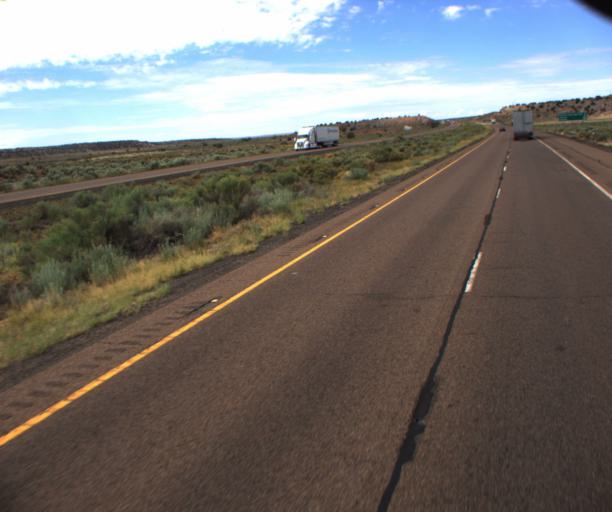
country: US
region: Arizona
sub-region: Apache County
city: Houck
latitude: 35.1865
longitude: -109.4491
